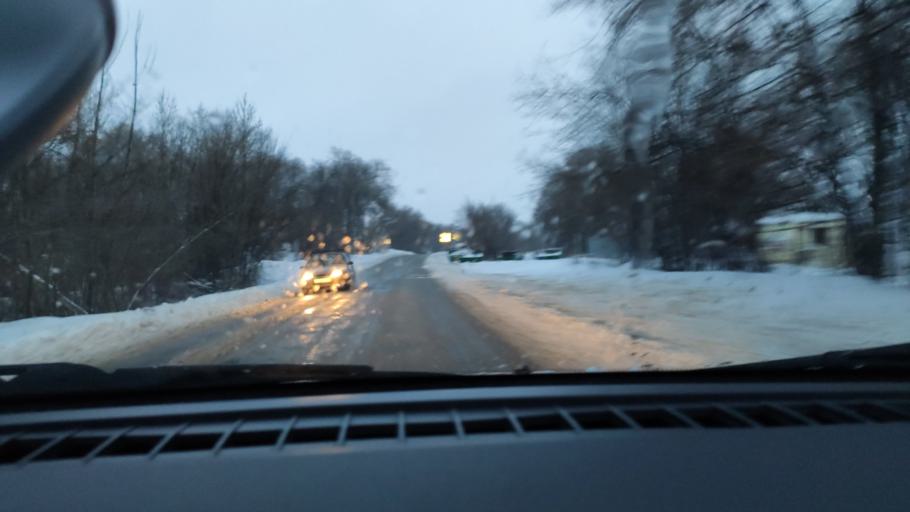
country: RU
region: Samara
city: Samara
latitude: 53.1180
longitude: 50.2305
